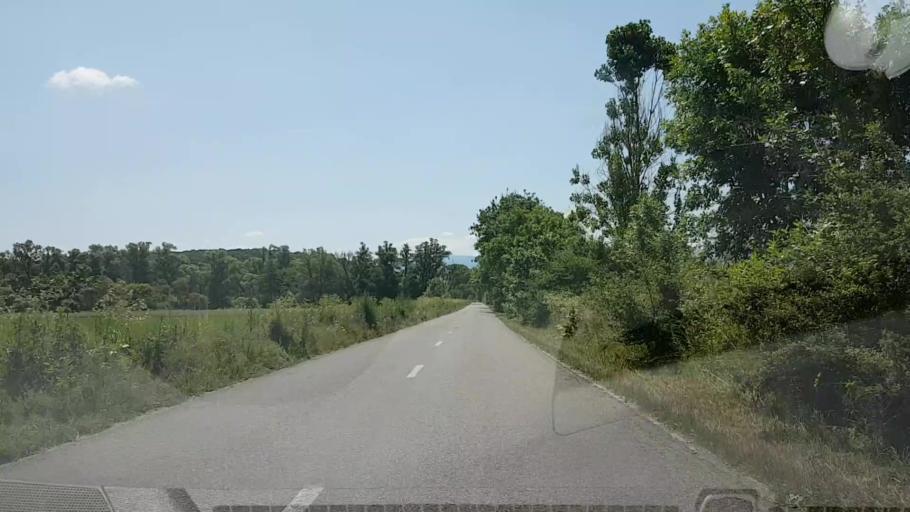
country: RO
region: Brasov
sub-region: Comuna Voila
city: Voila
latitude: 45.8577
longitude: 24.8284
